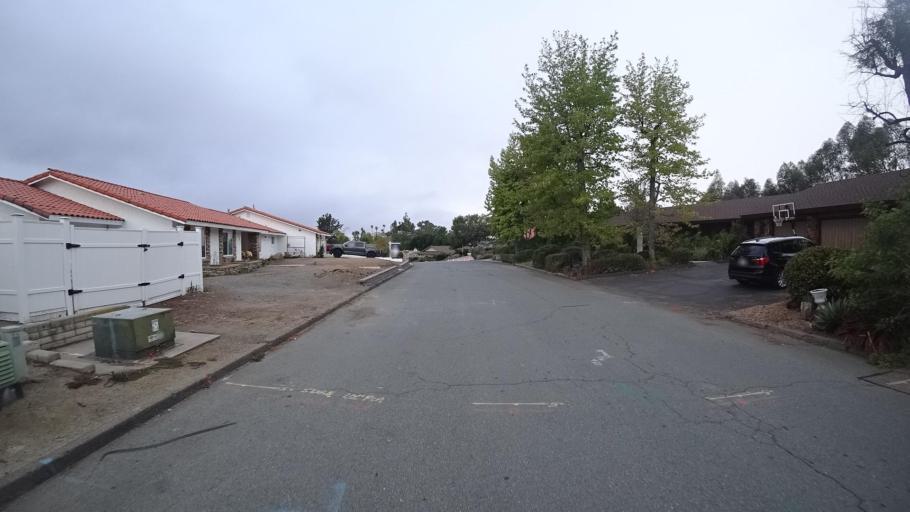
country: US
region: California
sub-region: San Diego County
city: Granite Hills
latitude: 32.7755
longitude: -116.9143
